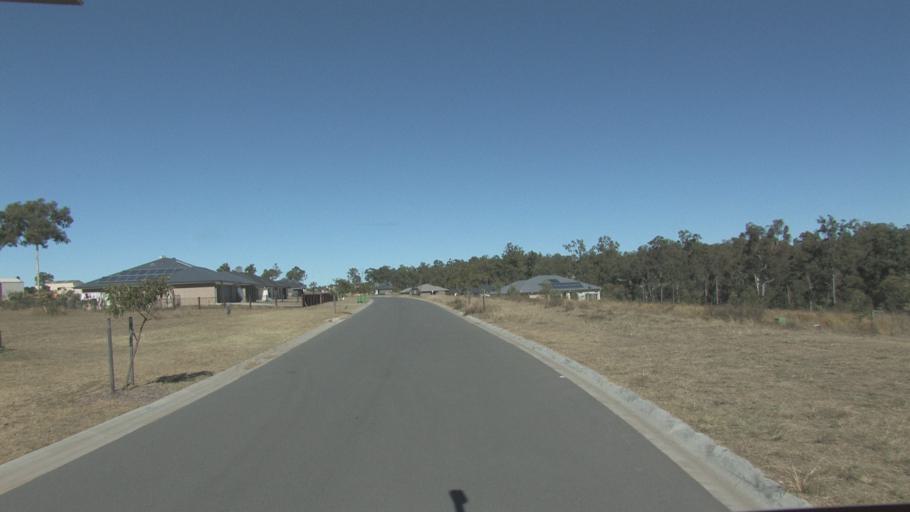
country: AU
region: Queensland
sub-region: Logan
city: North Maclean
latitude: -27.7506
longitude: 152.9441
